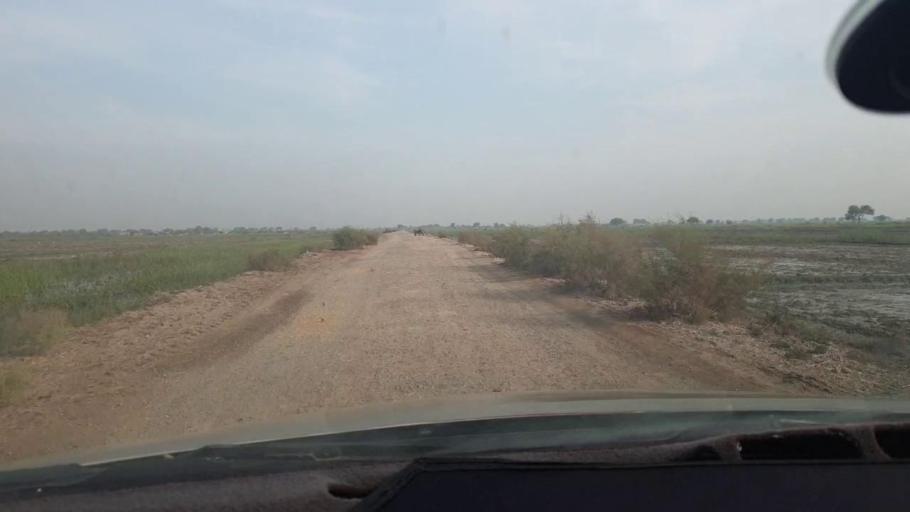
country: PK
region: Balochistan
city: Jhatpat
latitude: 28.3580
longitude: 68.4079
